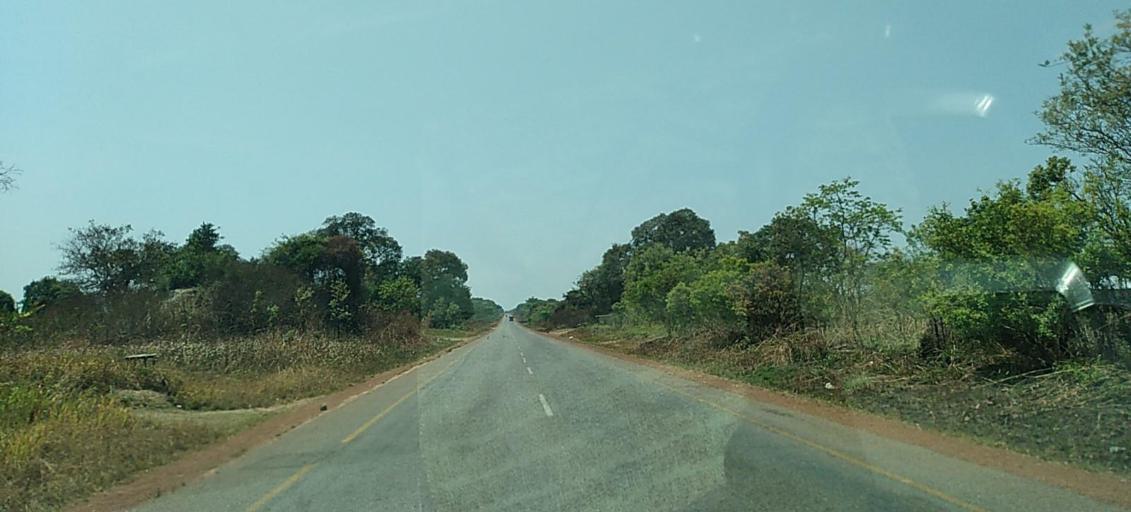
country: ZM
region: North-Western
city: Solwezi
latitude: -12.3811
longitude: 26.1924
